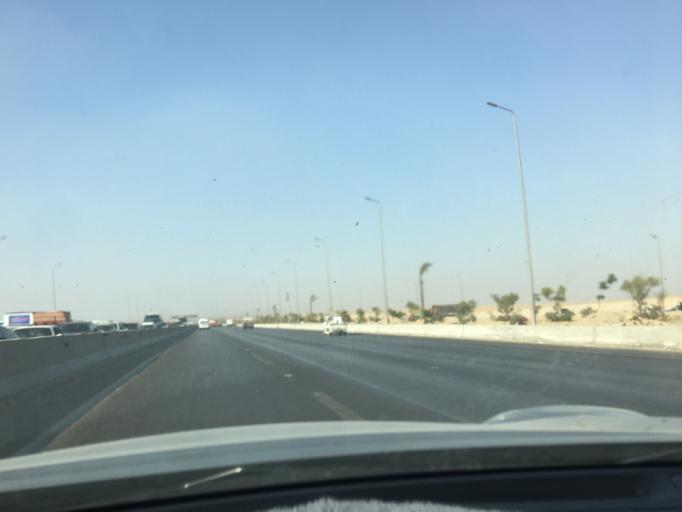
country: EG
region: Muhafazat al Qalyubiyah
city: Al Khankah
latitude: 30.0953
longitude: 31.4437
